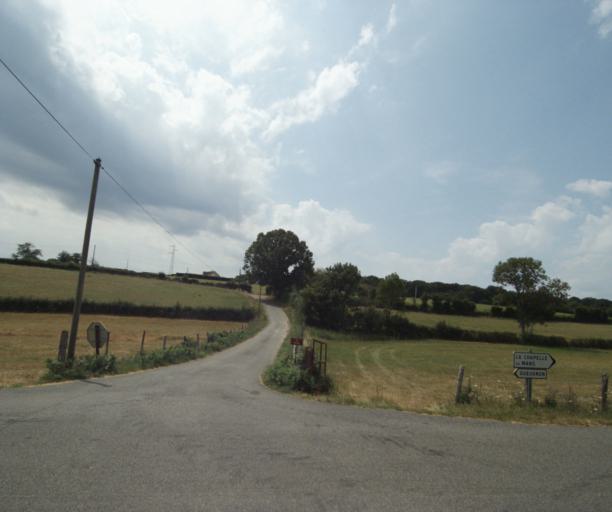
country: FR
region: Bourgogne
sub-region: Departement de Saone-et-Loire
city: Gueugnon
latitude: 46.6058
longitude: 4.0013
